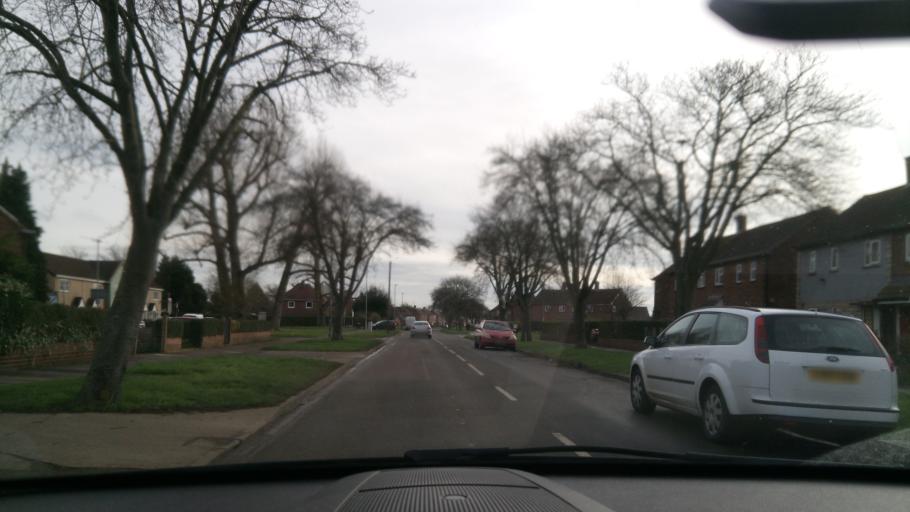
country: GB
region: England
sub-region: Peterborough
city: Peterborough
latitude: 52.5989
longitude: -0.2268
